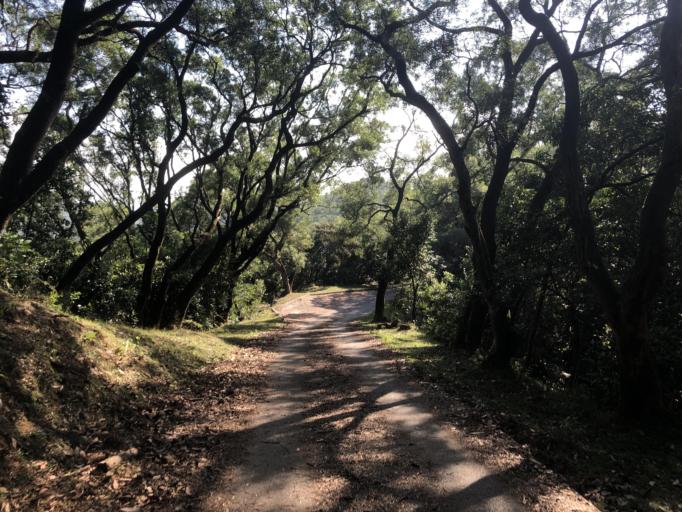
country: HK
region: Tsuen Wan
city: Tsuen Wan
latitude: 22.3938
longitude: 114.0863
